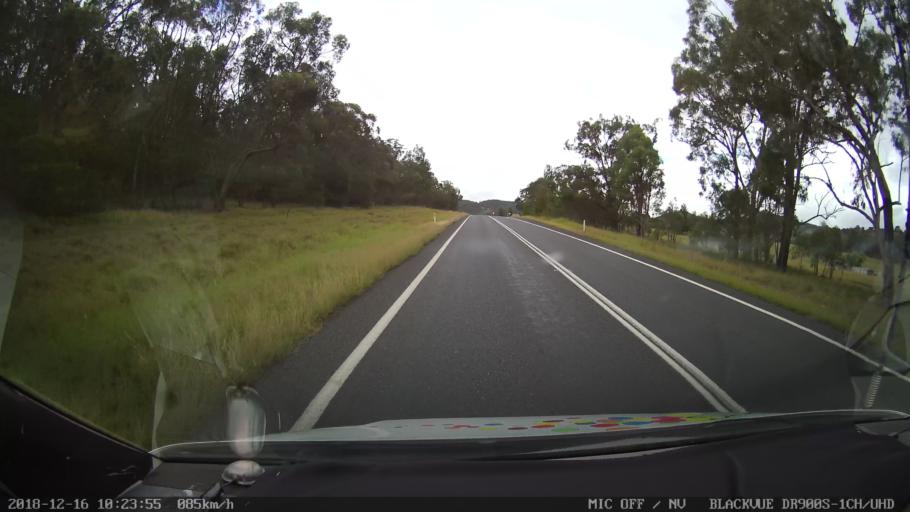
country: AU
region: New South Wales
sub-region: Tenterfield Municipality
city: Carrolls Creek
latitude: -29.1766
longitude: 152.0056
